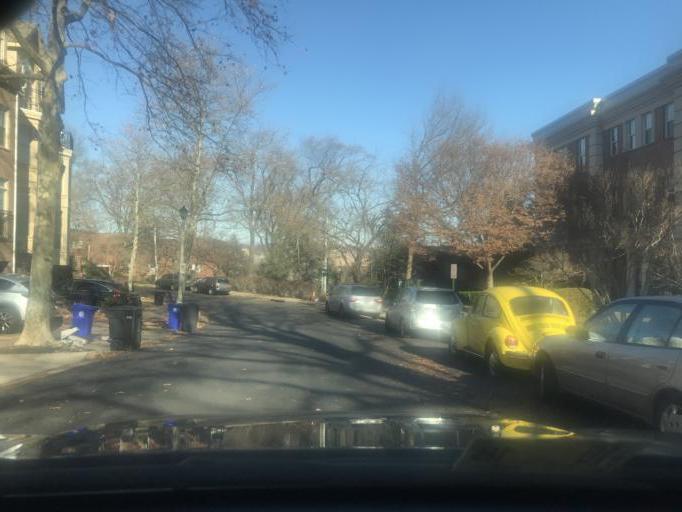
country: US
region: Virginia
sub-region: Arlington County
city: Arlington
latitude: 38.8974
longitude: -77.0741
